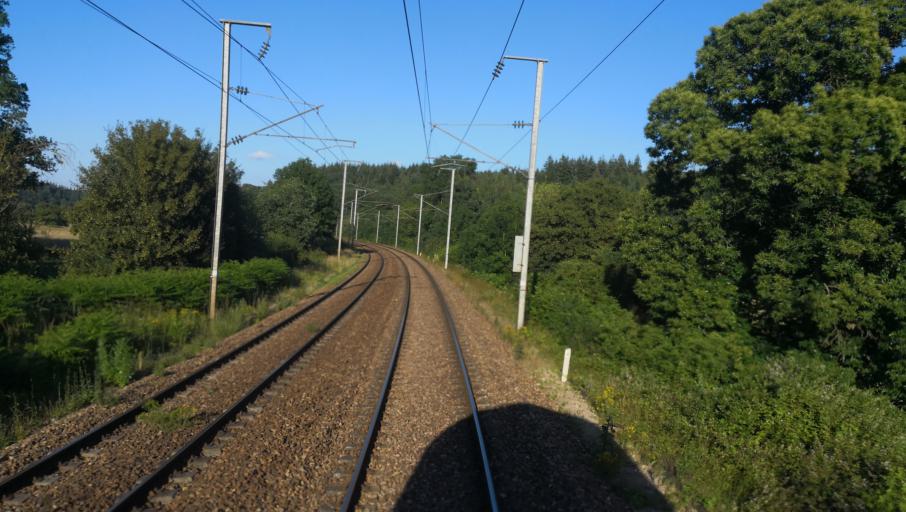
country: FR
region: Haute-Normandie
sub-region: Departement de l'Eure
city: Conches-en-Ouche
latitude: 48.9745
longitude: 0.9798
